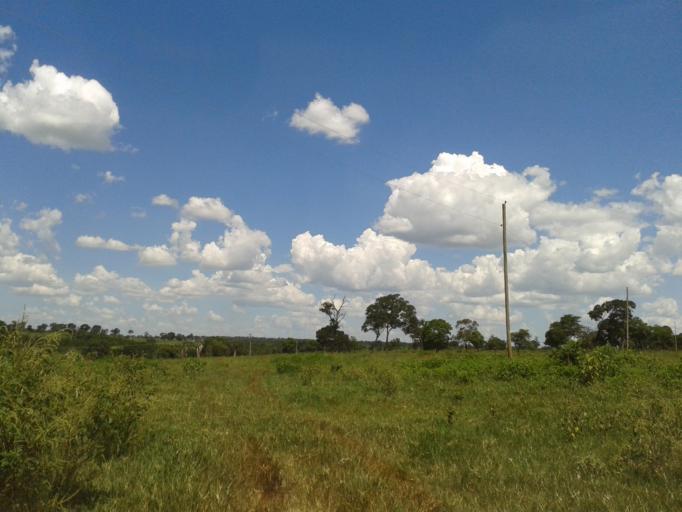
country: BR
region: Minas Gerais
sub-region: Santa Vitoria
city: Santa Vitoria
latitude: -19.1466
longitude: -50.5400
